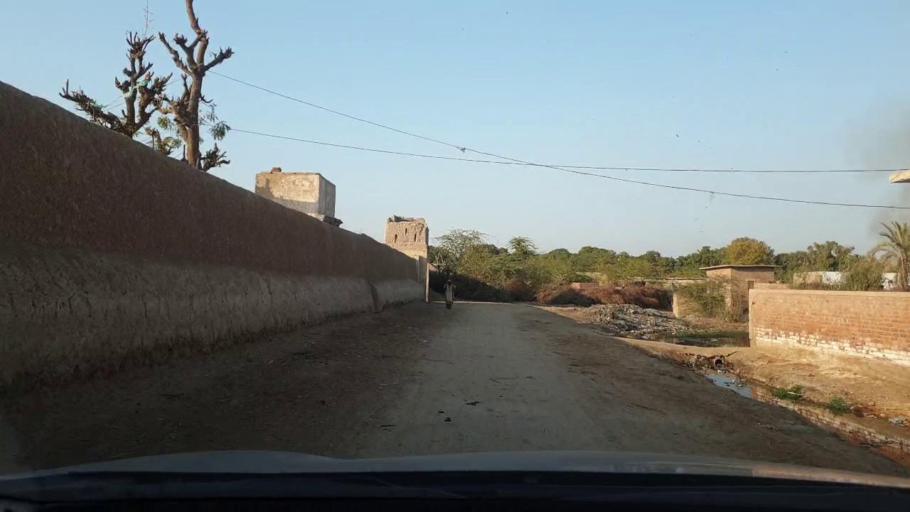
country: PK
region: Sindh
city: Berani
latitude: 25.6357
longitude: 68.8102
